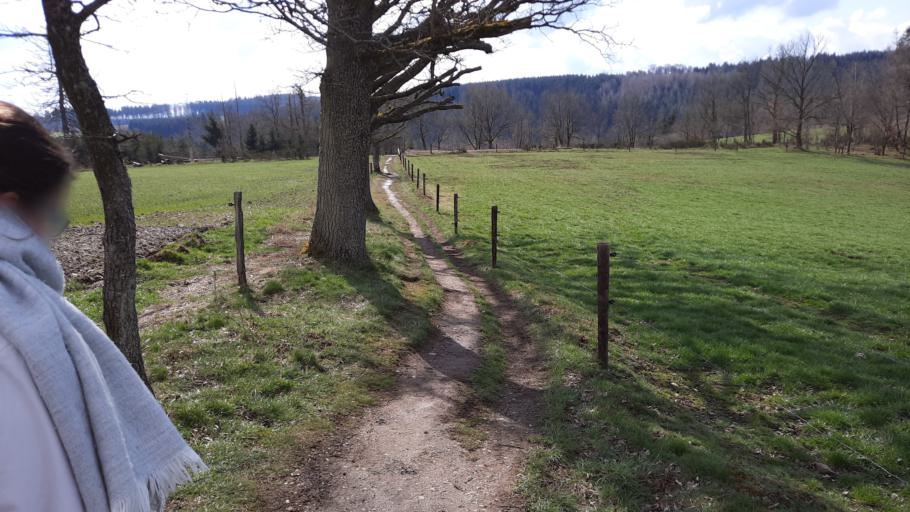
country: BE
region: Wallonia
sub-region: Province du Luxembourg
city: Houffalize
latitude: 50.1357
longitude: 5.8063
